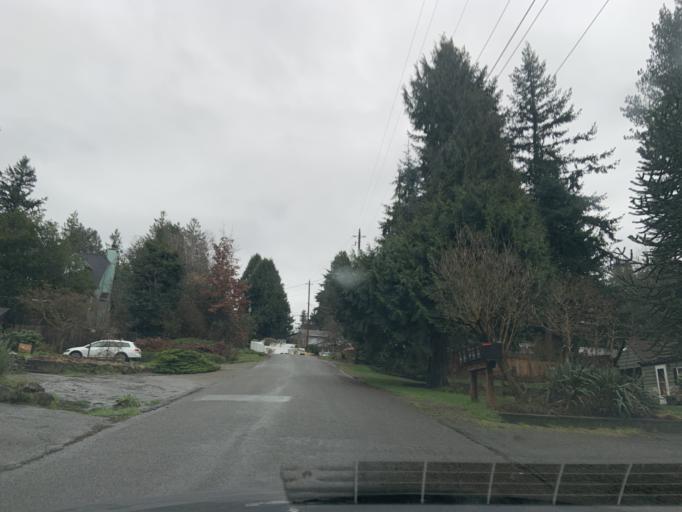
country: US
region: Washington
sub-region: King County
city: Lake Forest Park
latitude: 47.7100
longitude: -122.2847
